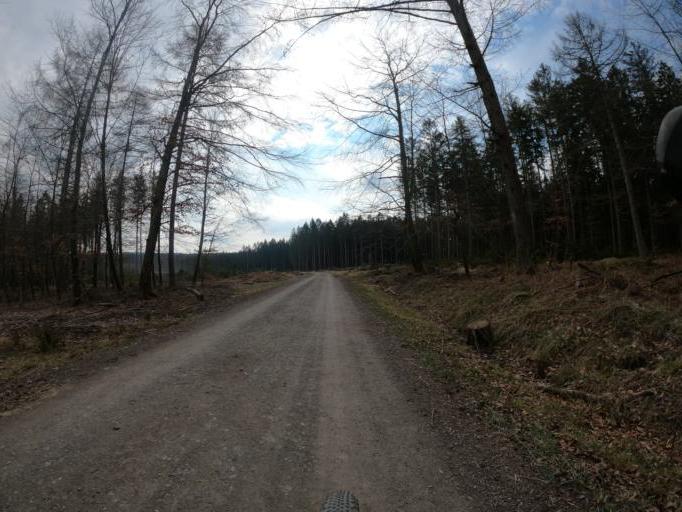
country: DE
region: North Rhine-Westphalia
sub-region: Regierungsbezirk Koln
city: Roetgen
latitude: 50.6498
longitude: 6.2425
